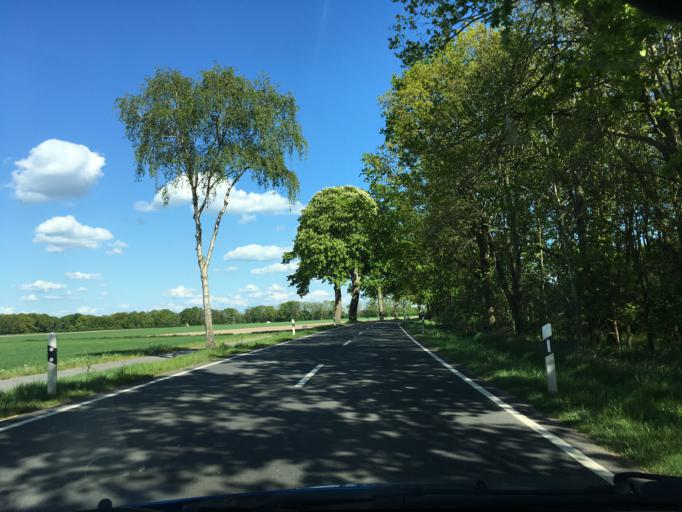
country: DE
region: Lower Saxony
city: Gartow
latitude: 53.0272
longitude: 11.4768
